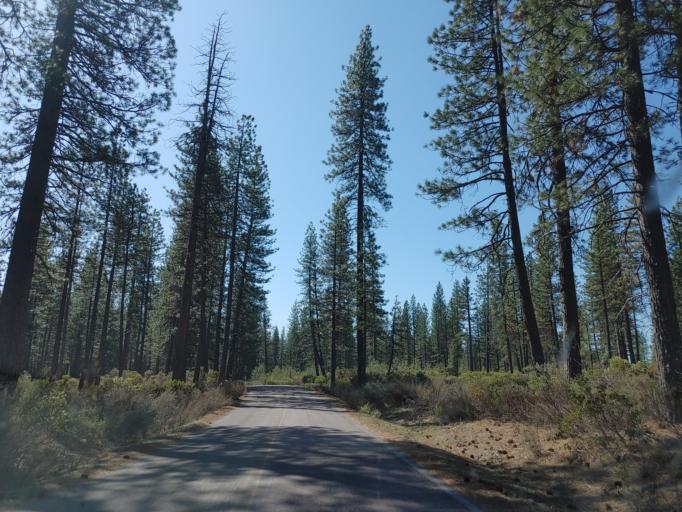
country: US
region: California
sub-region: Siskiyou County
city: McCloud
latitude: 41.2546
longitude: -122.0303
